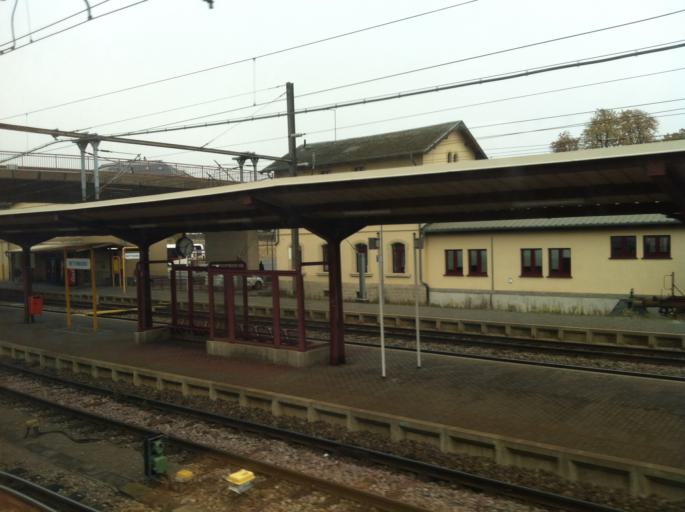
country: LU
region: Luxembourg
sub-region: Canton d'Esch-sur-Alzette
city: Bettembourg
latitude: 49.5158
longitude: 6.1012
